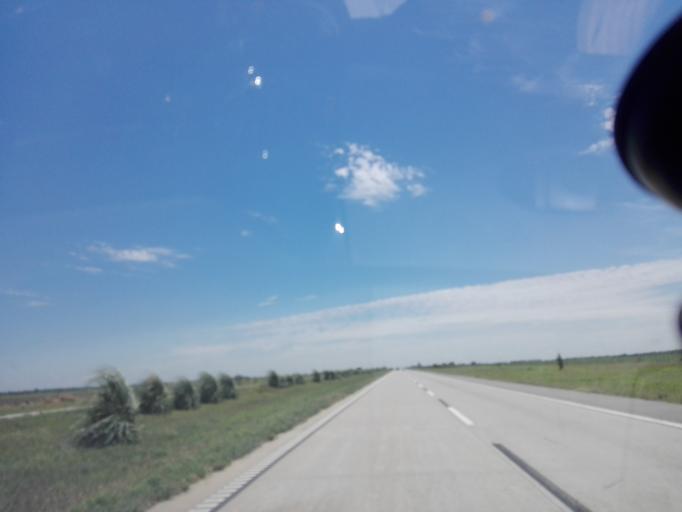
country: AR
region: Cordoba
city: Villa Maria
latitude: -32.4436
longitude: -63.1127
